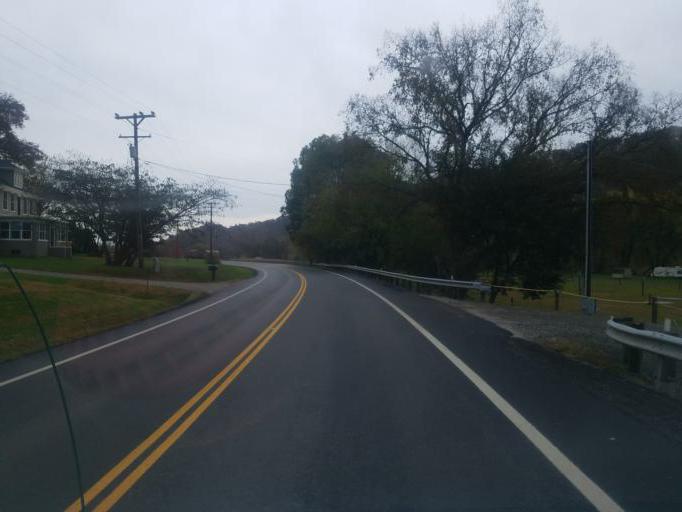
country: US
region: Ohio
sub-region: Washington County
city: Devola
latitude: 39.5313
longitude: -81.5404
